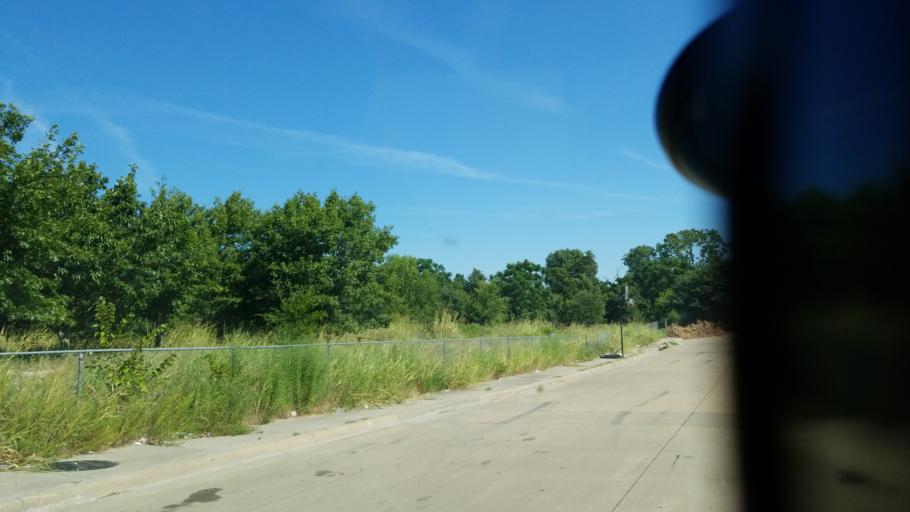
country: US
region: Texas
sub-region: Dallas County
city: Cockrell Hill
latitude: 32.6770
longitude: -96.8272
